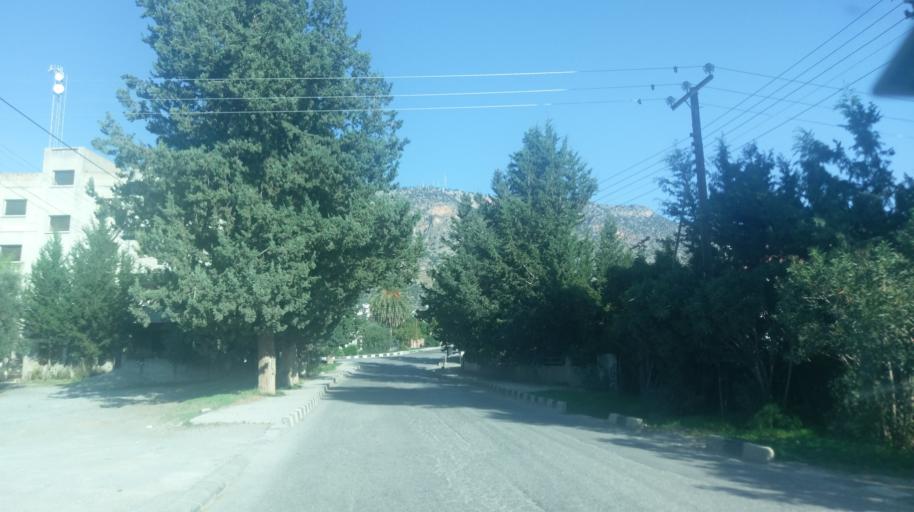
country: CY
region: Keryneia
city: Kyrenia
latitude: 35.2882
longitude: 33.2795
